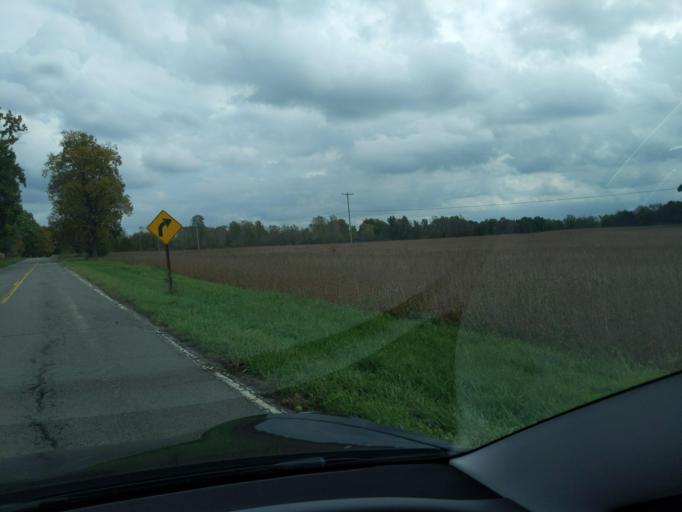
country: US
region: Michigan
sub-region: Ingham County
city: Leslie
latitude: 42.4127
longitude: -84.3594
